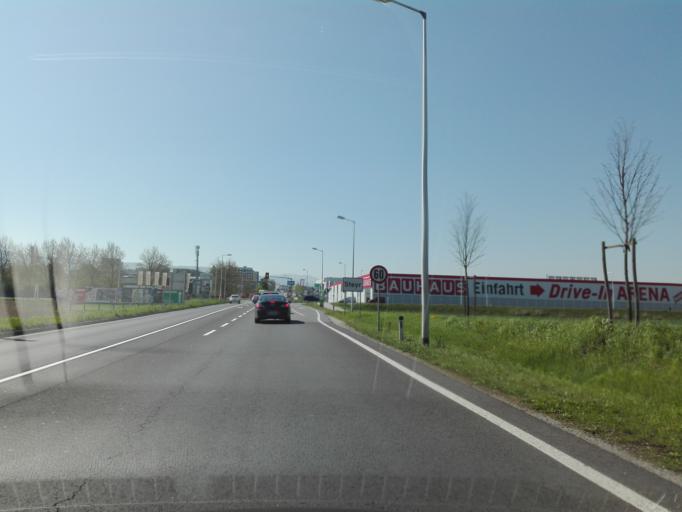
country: AT
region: Upper Austria
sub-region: Steyr Stadt
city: Steyr
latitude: 48.0653
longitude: 14.4211
